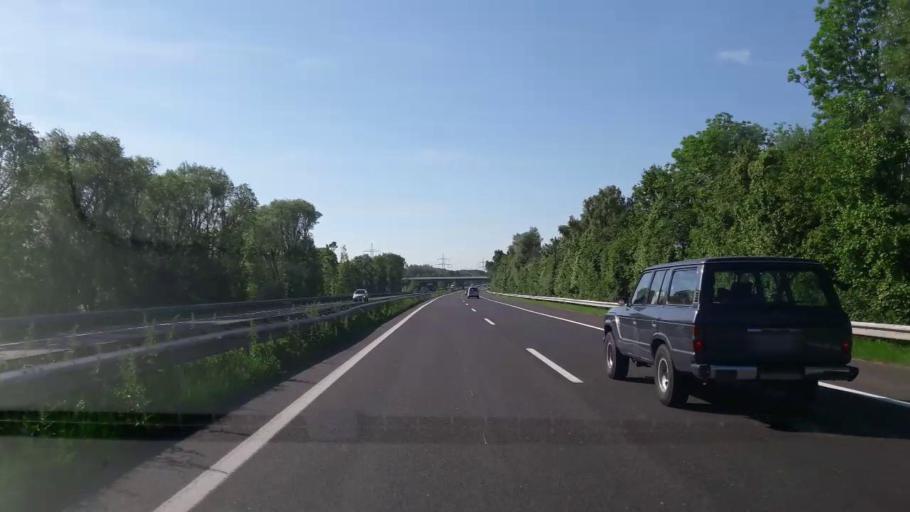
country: AT
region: Burgenland
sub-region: Eisenstadt-Umgebung
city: Wimpassing an der Leitha
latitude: 47.9106
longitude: 16.4097
